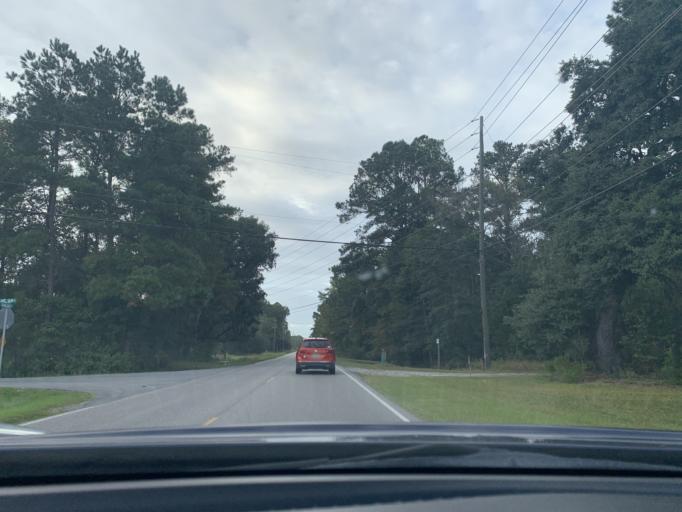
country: US
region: Georgia
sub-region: Chatham County
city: Pooler
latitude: 32.0603
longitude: -81.2704
